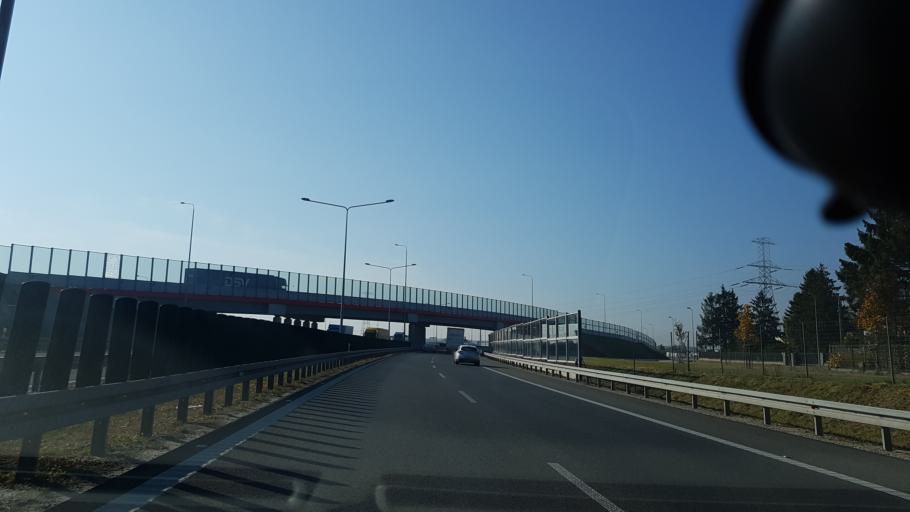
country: PL
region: Masovian Voivodeship
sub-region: Powiat pruszkowski
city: Nowe Grocholice
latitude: 52.1251
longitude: 20.8761
